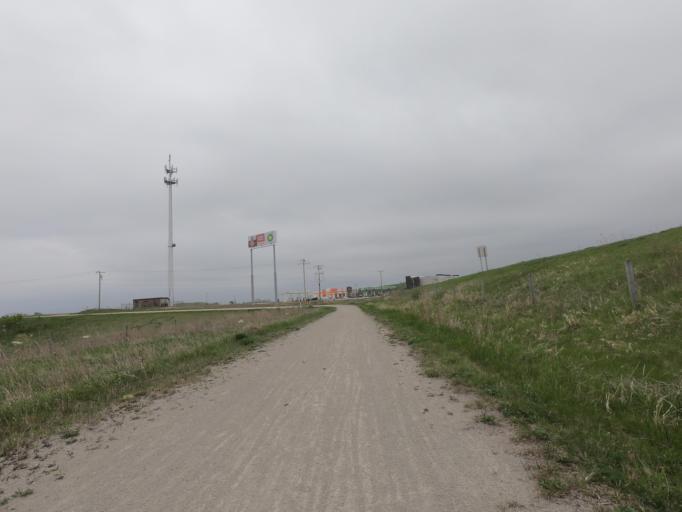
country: US
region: Wisconsin
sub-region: Jefferson County
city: Jefferson
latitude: 43.0327
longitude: -88.8038
